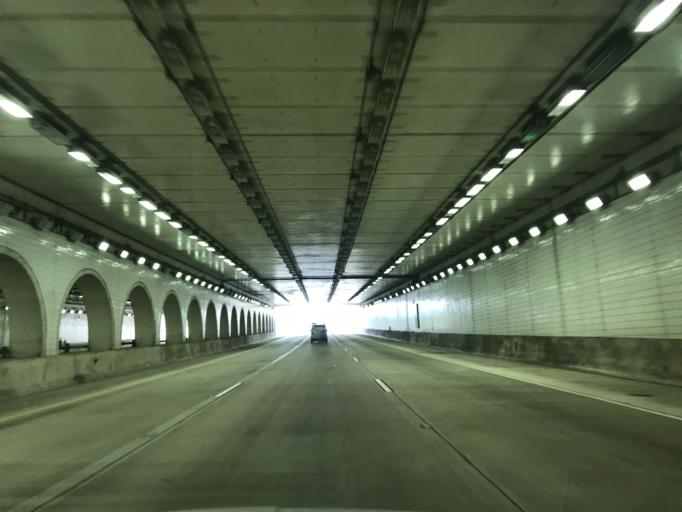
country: US
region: Maryland
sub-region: Montgomery County
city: Redland
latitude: 39.1380
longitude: -77.1339
